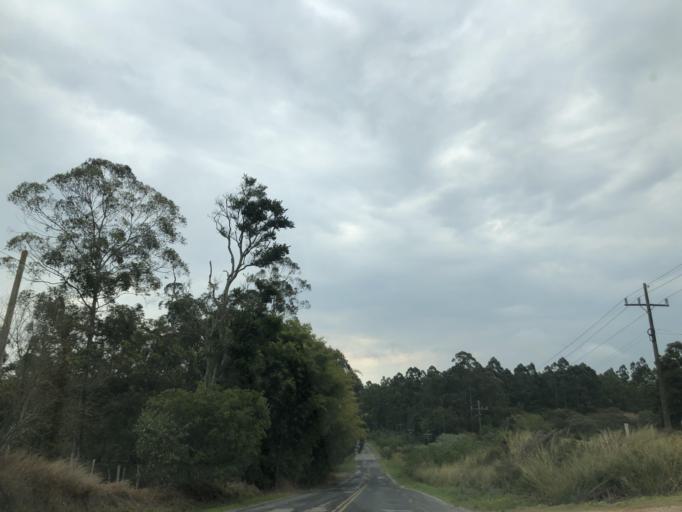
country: BR
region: Sao Paulo
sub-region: Pilar Do Sul
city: Pilar do Sul
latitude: -23.8128
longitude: -47.6411
